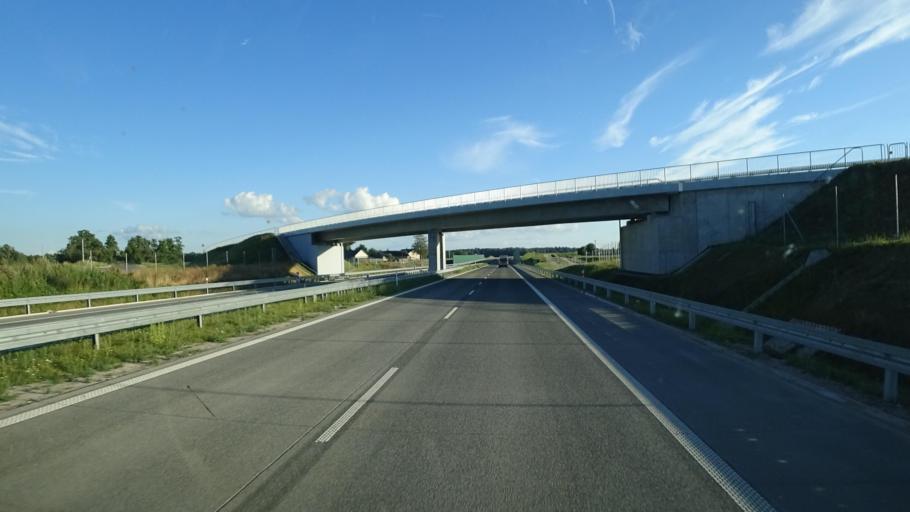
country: PL
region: Podlasie
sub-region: Powiat suwalski
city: Raczki
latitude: 53.9432
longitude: 22.7641
